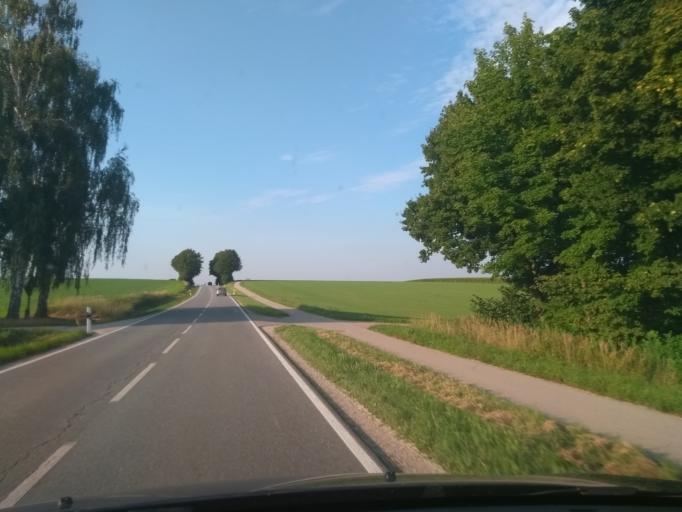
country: DE
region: Bavaria
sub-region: Upper Bavaria
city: Markt Indersdorf
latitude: 48.3325
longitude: 11.3881
